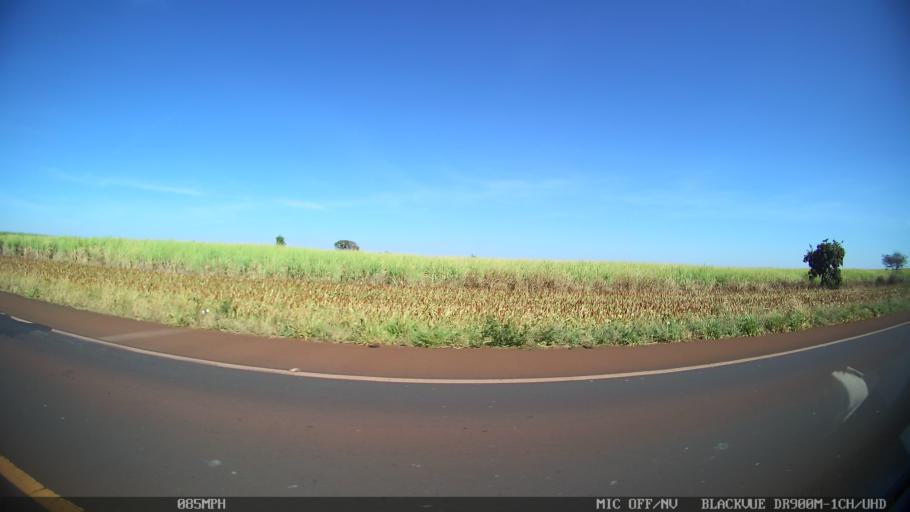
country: BR
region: Sao Paulo
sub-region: Ipua
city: Ipua
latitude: -20.4667
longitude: -48.1234
